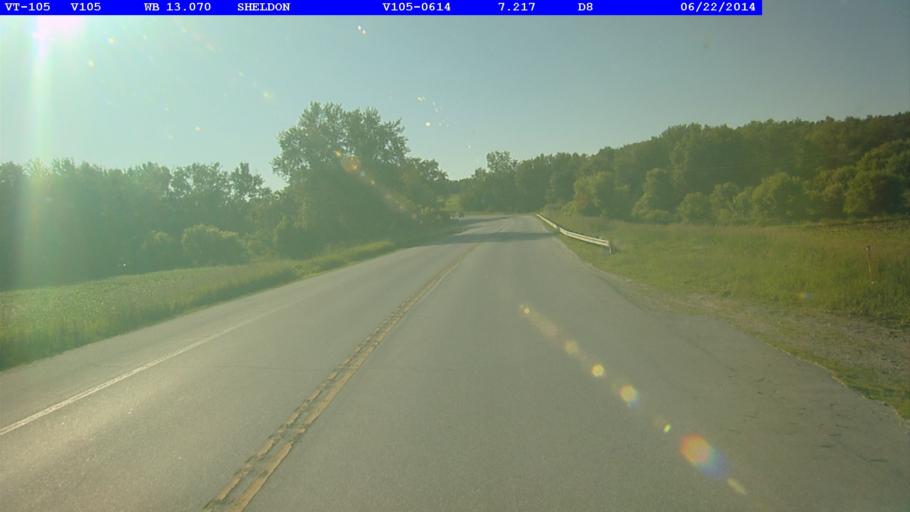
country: US
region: Vermont
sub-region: Franklin County
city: Enosburg Falls
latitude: 44.9105
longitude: -72.8956
